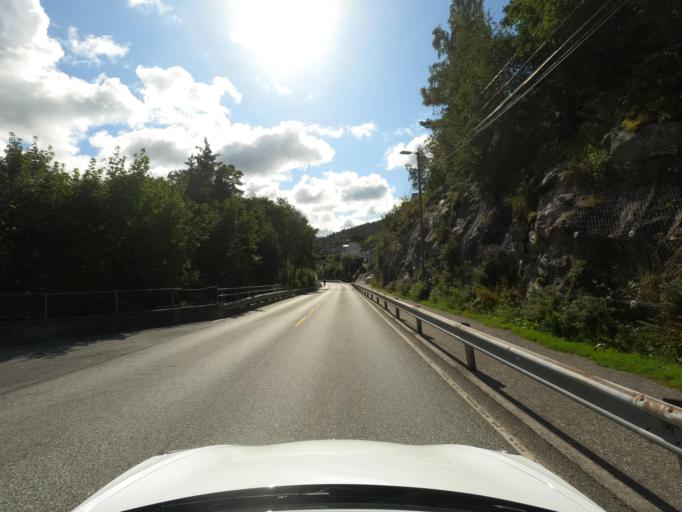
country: NO
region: Hordaland
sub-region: Bergen
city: Bergen
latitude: 60.4405
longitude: 5.3007
